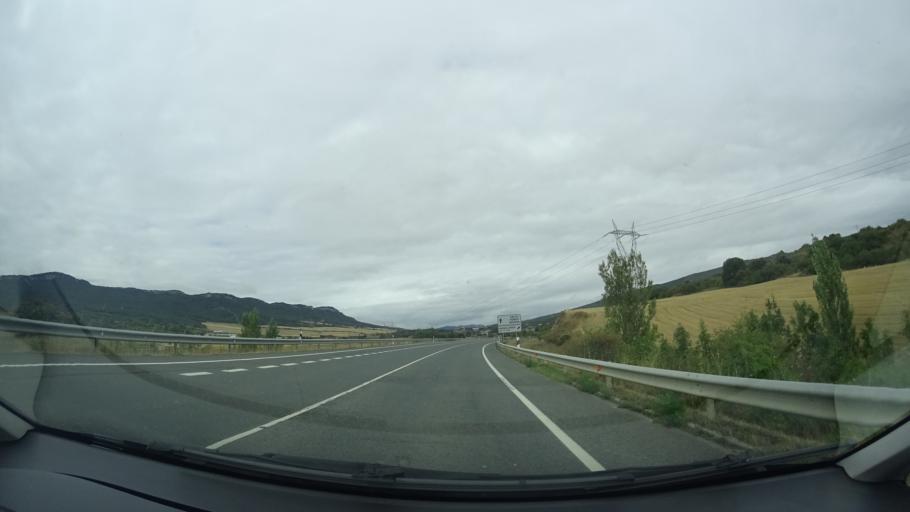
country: ES
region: Basque Country
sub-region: Provincia de Alava
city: Arminon
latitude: 42.8124
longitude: -2.8174
